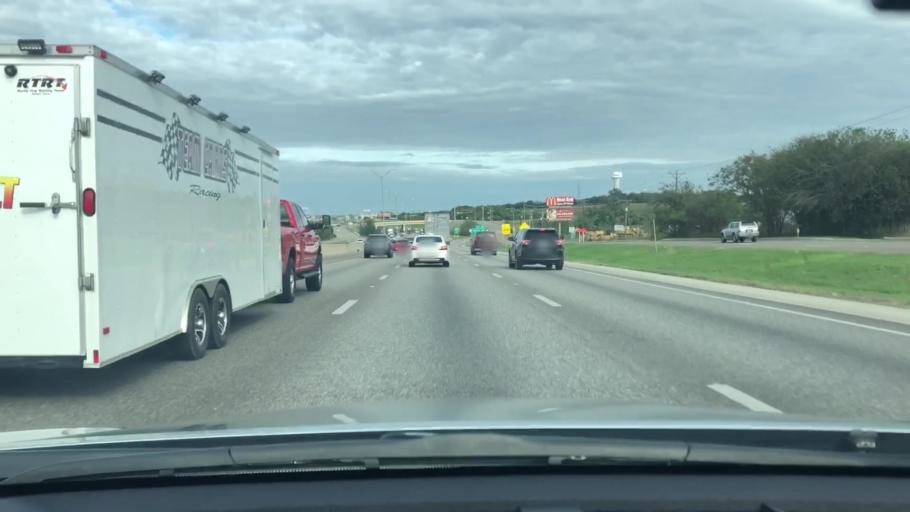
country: US
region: Texas
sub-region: Guadalupe County
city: Northcliff
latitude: 29.6604
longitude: -98.1753
